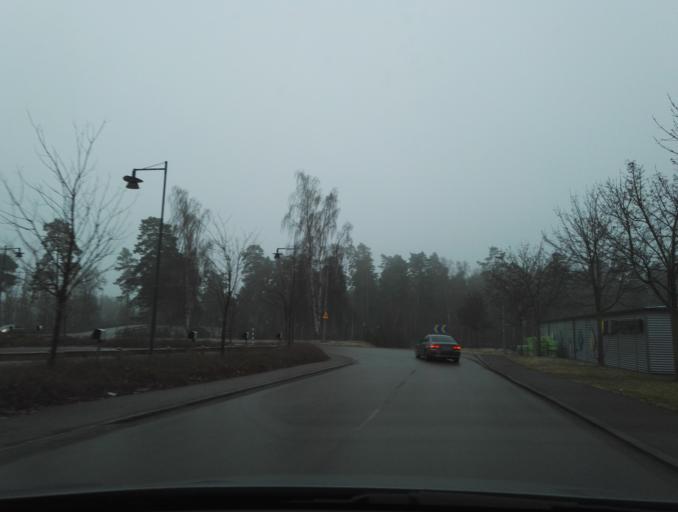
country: SE
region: Kronoberg
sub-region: Vaxjo Kommun
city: Vaexjoe
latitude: 56.8771
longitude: 14.7755
